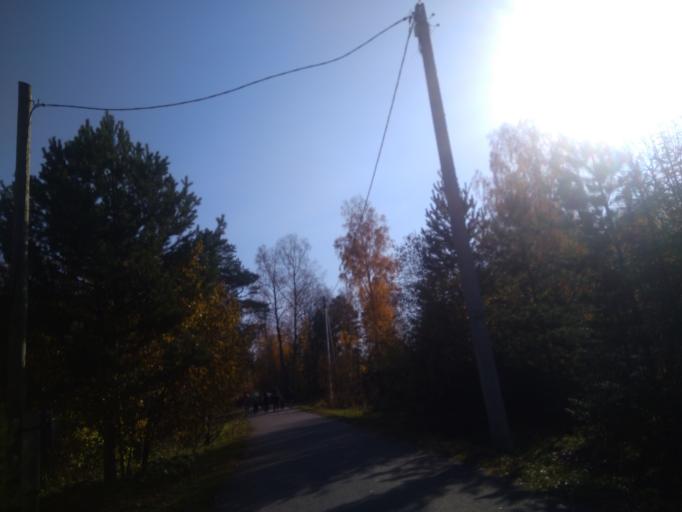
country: RU
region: Sverdlovsk
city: Mikhaylovsk
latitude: 56.5236
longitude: 59.2318
